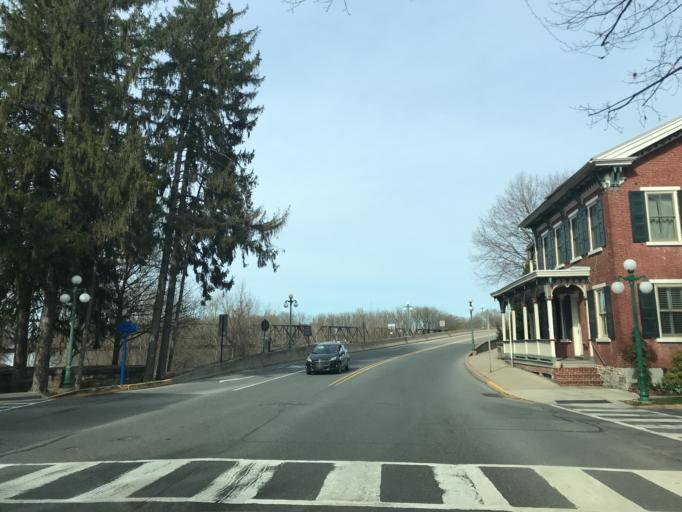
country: US
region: Pennsylvania
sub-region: Union County
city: Lewisburg
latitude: 40.9662
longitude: -76.8817
